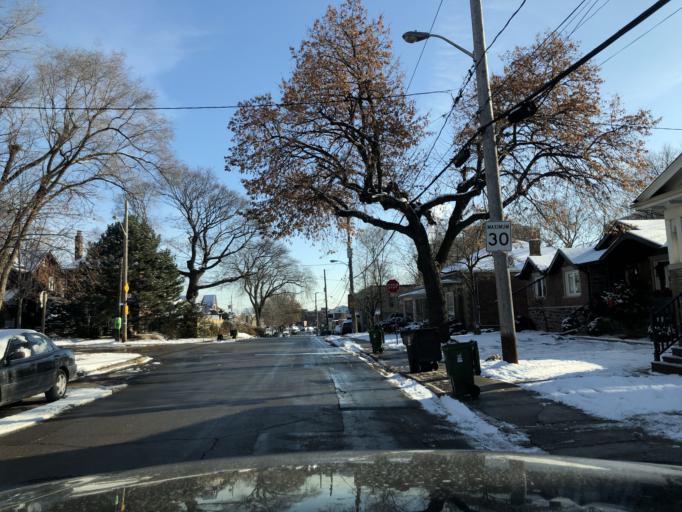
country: CA
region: Ontario
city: Etobicoke
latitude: 43.7026
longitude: -79.5160
